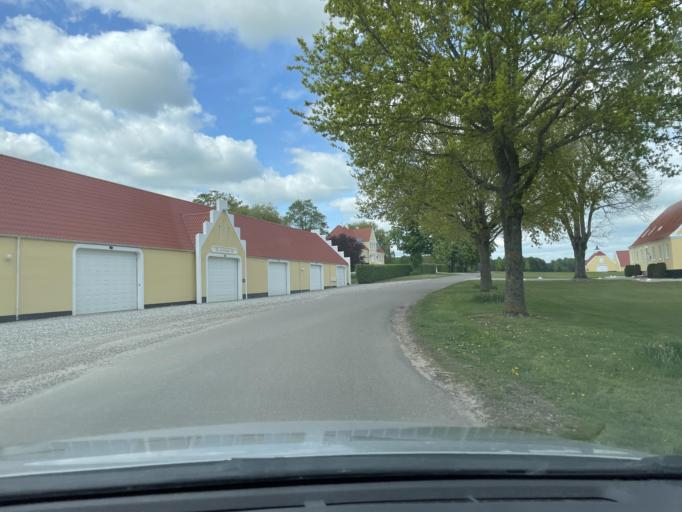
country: DK
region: Central Jutland
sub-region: Odder Kommune
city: Odder
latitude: 55.9101
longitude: 10.1019
